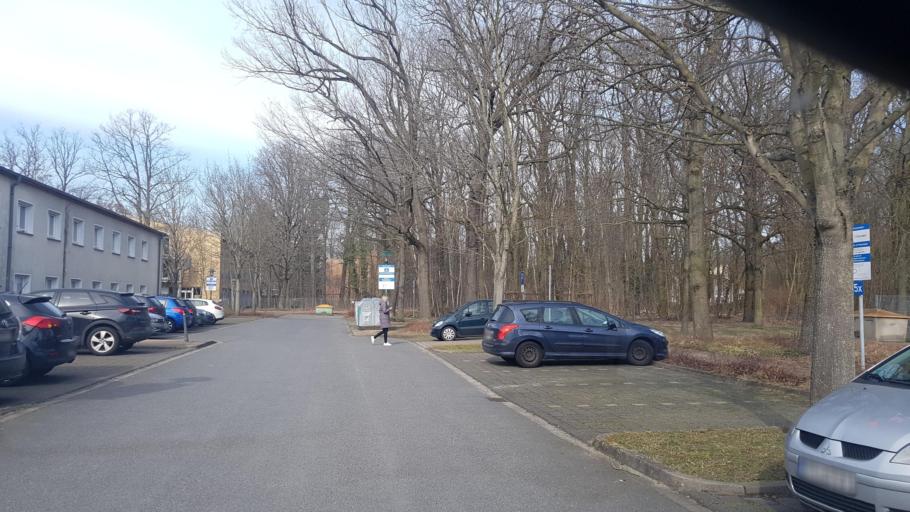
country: DE
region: Berlin
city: Wannsee
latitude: 52.3837
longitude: 13.1409
